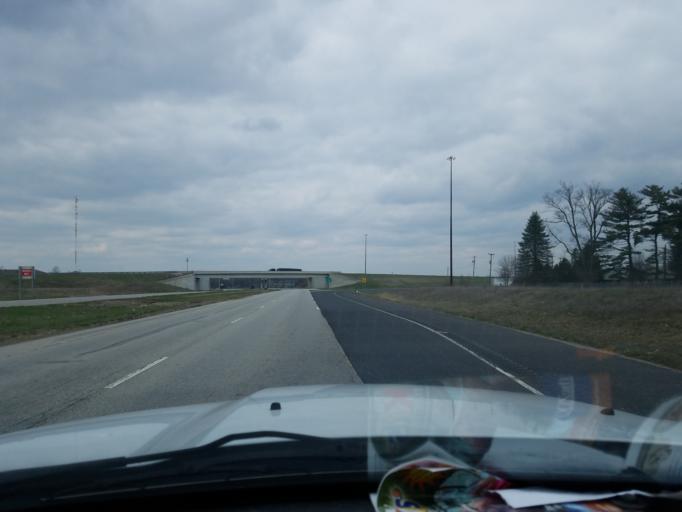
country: US
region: Indiana
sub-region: Vigo County
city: Terre Haute
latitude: 39.3671
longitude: -87.3880
